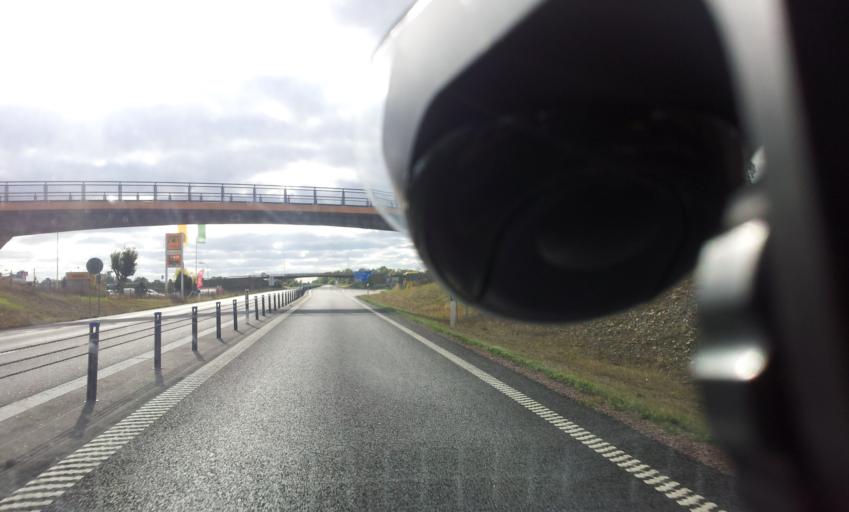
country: SE
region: Kalmar
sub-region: Kalmar Kommun
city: Lindsdal
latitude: 56.7975
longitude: 16.3563
